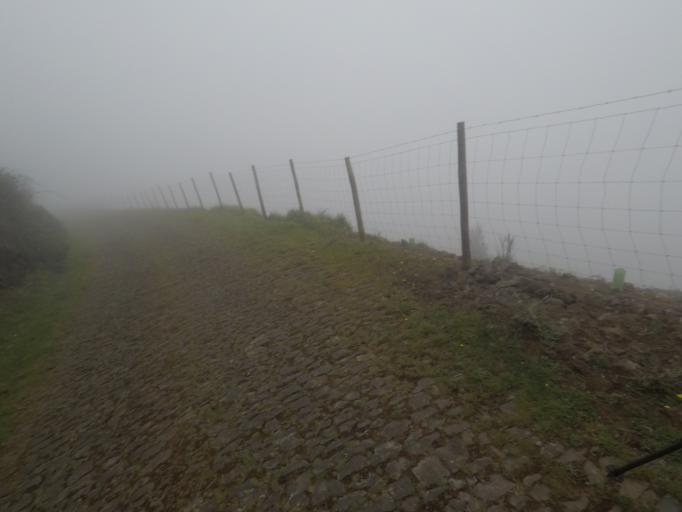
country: PT
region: Madeira
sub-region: Calheta
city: Arco da Calheta
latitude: 32.7328
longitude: -17.0970
